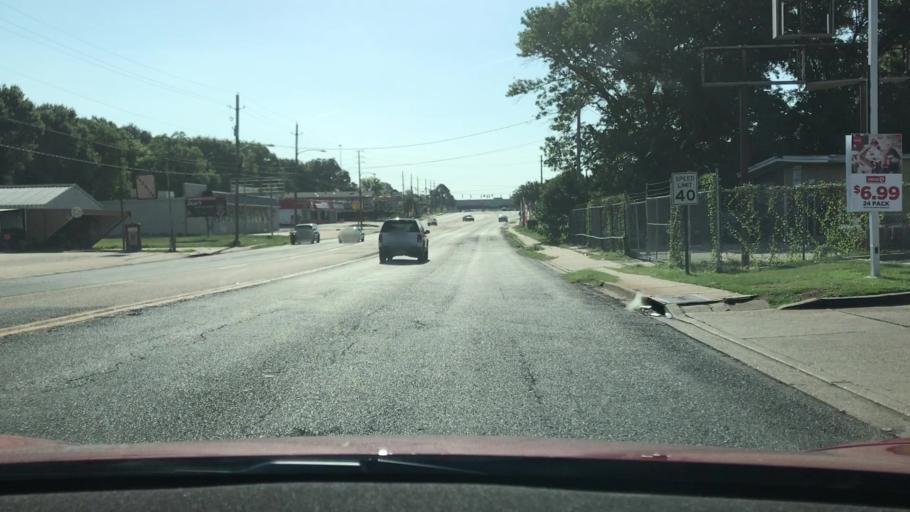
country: US
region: Louisiana
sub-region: Bossier Parish
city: Bossier City
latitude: 32.4420
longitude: -93.7625
